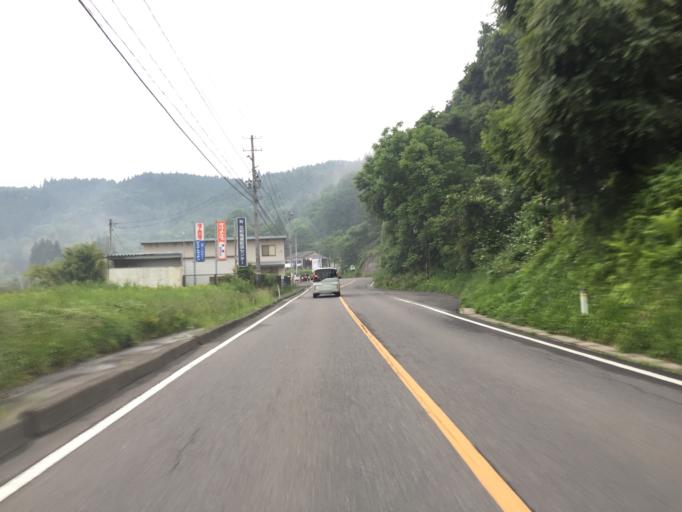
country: JP
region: Fukushima
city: Ishikawa
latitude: 37.1572
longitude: 140.4653
